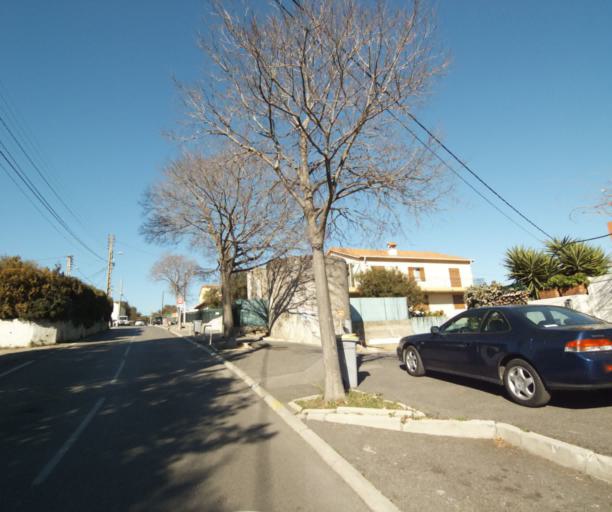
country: FR
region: Provence-Alpes-Cote d'Azur
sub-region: Departement des Alpes-Maritimes
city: Biot
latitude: 43.5999
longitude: 7.1028
